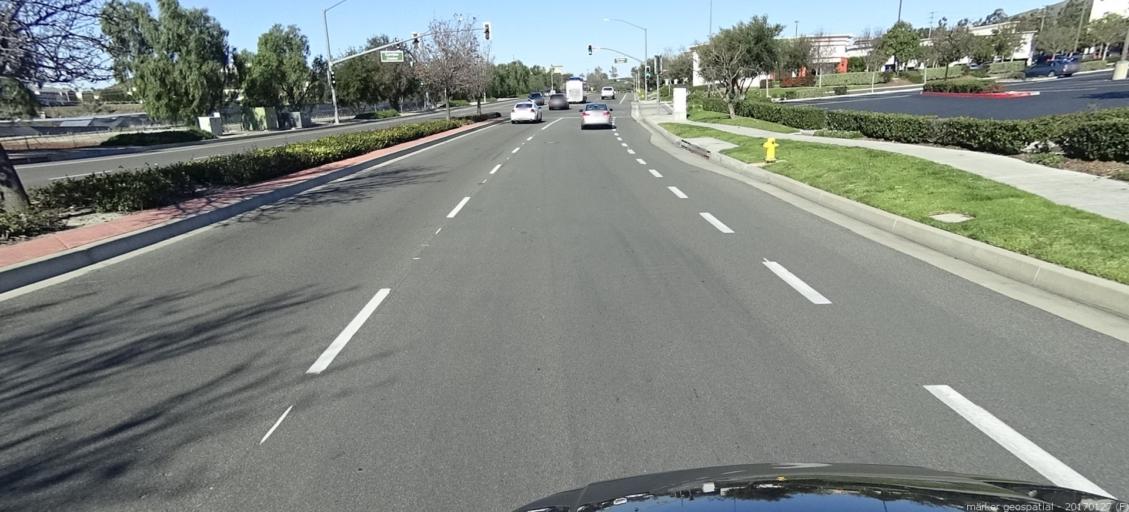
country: US
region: California
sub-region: Orange County
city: Foothill Ranch
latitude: 33.6705
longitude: -117.6637
